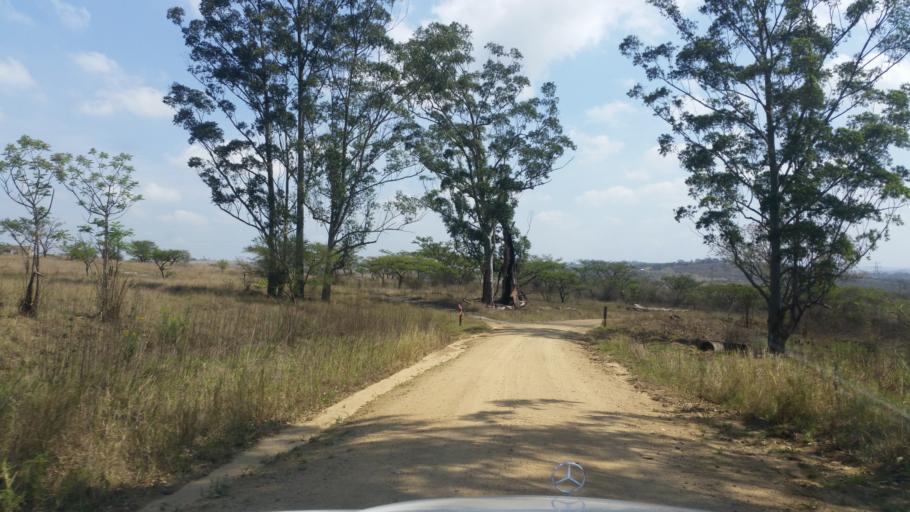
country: ZA
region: KwaZulu-Natal
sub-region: uMgungundlovu District Municipality
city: Camperdown
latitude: -29.7046
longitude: 30.4894
